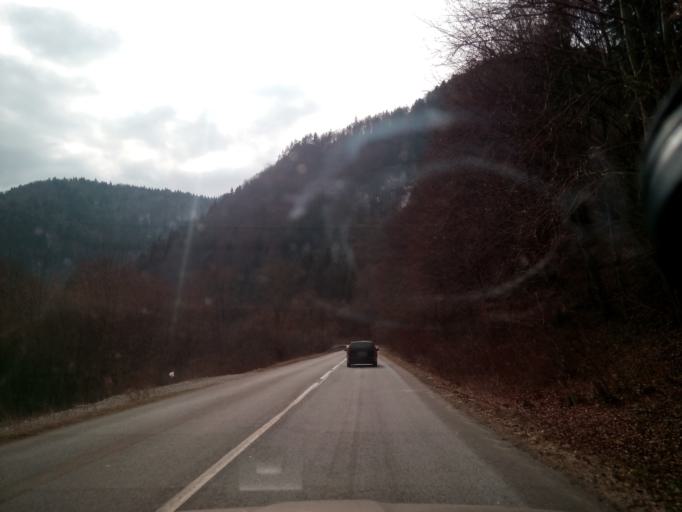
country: SK
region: Zilinsky
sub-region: Okres Zilina
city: Terchova
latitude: 49.2373
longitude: 19.1537
